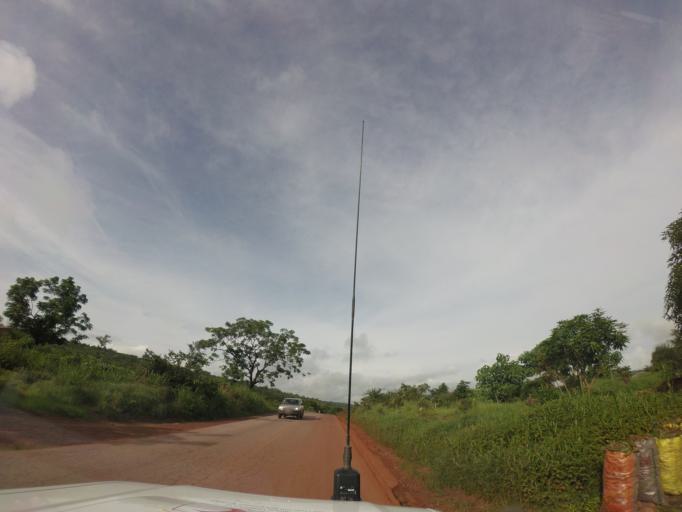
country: GN
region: Kindia
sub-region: Kindia
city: Kindia
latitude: 9.8482
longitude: -13.0917
